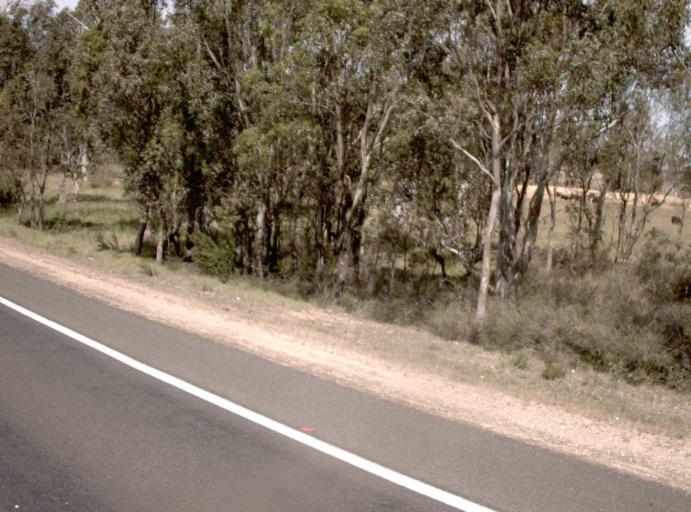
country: AU
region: Victoria
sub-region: East Gippsland
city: Bairnsdale
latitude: -37.8972
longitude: 147.3658
